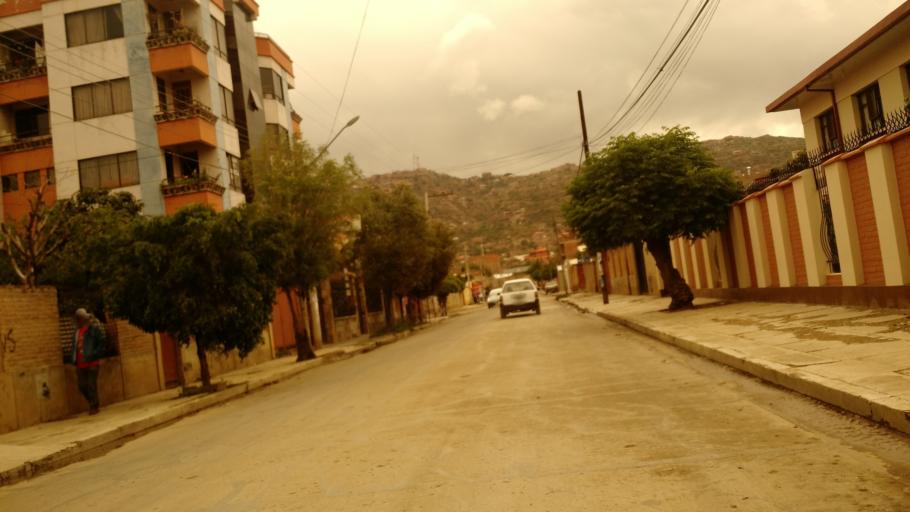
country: BO
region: Cochabamba
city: Cochabamba
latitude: -17.4326
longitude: -66.1552
